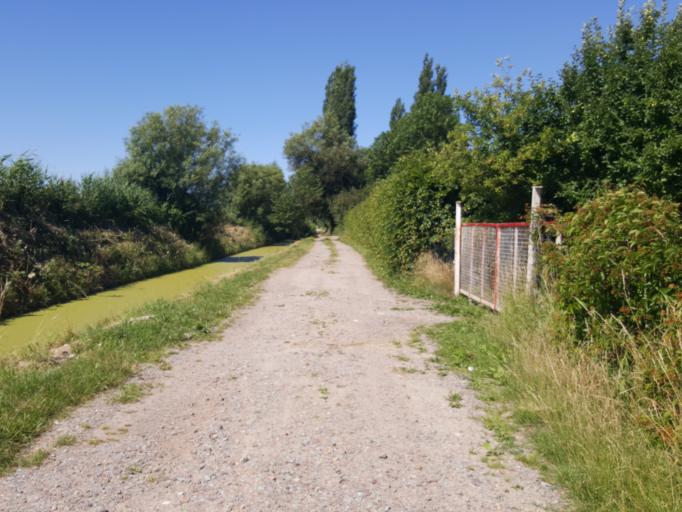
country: DE
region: Hamburg
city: Bergedorf
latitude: 53.4771
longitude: 10.2172
